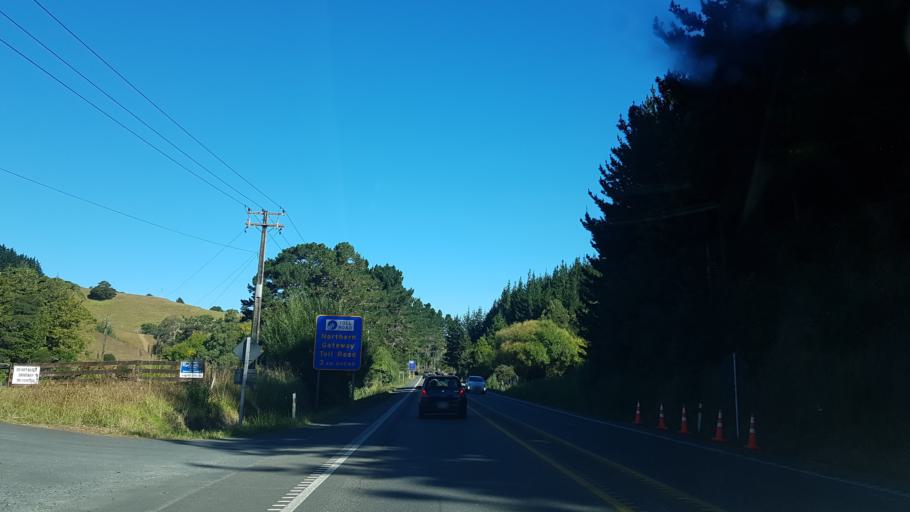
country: NZ
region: Auckland
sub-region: Auckland
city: Warkworth
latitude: -36.5048
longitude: 174.6698
